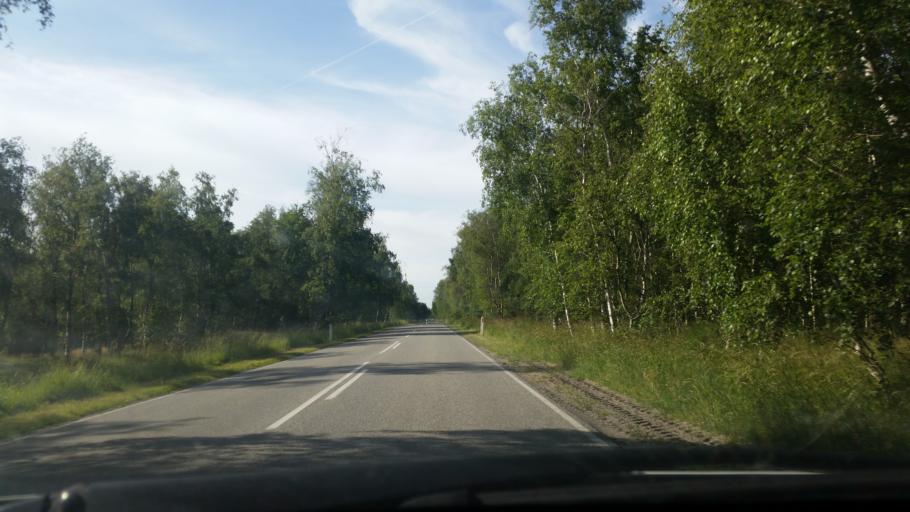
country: DK
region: Central Jutland
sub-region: Samso Kommune
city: Tranebjerg
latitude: 55.9318
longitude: 10.5841
